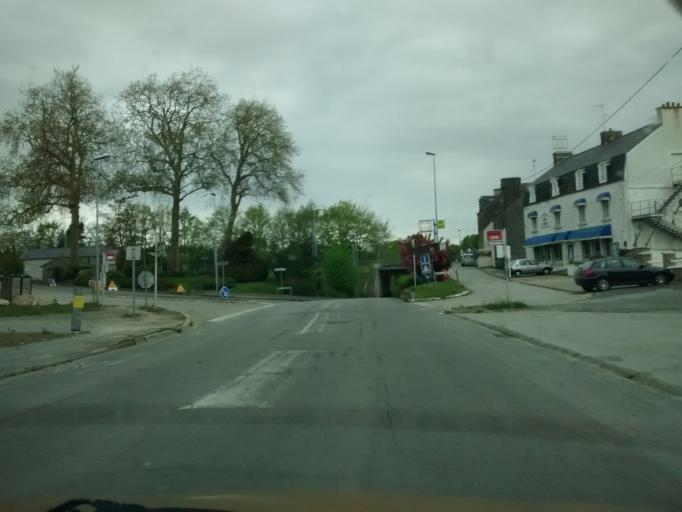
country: FR
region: Brittany
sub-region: Departement du Morbihan
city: Questembert
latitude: 47.6820
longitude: -2.4489
